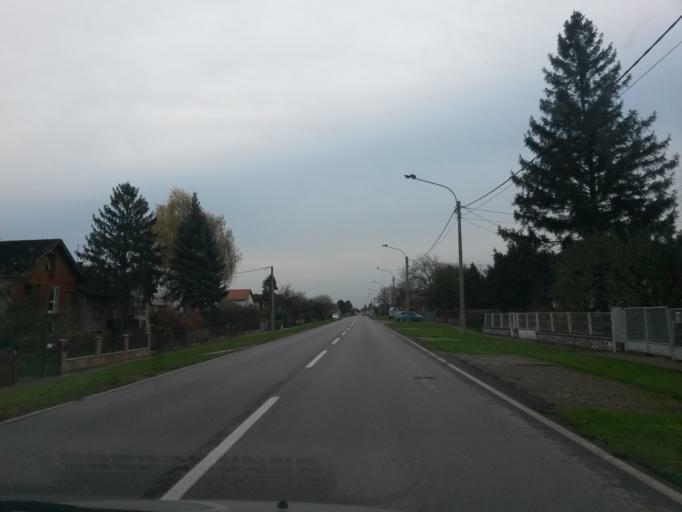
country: HR
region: Osjecko-Baranjska
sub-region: Grad Osijek
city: Bilje
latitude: 45.6111
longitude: 18.7371
